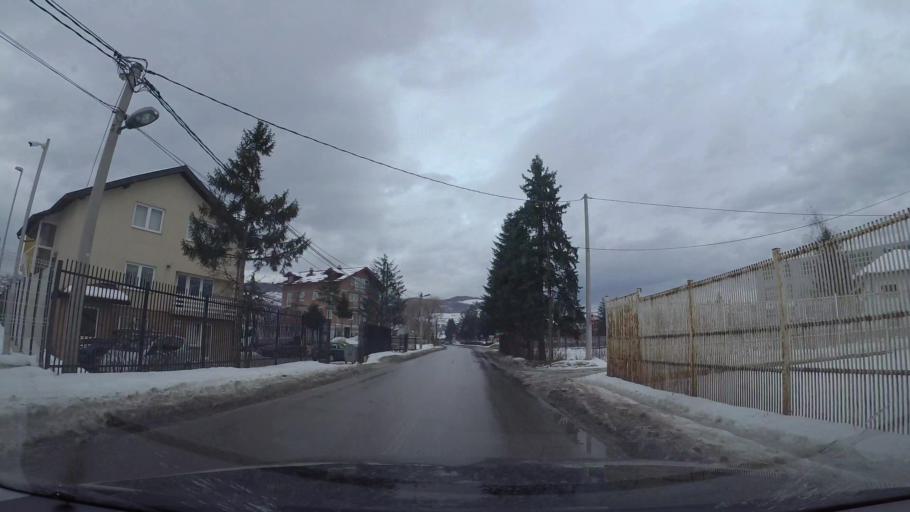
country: BA
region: Federation of Bosnia and Herzegovina
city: Vogosca
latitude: 43.8769
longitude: 18.3085
